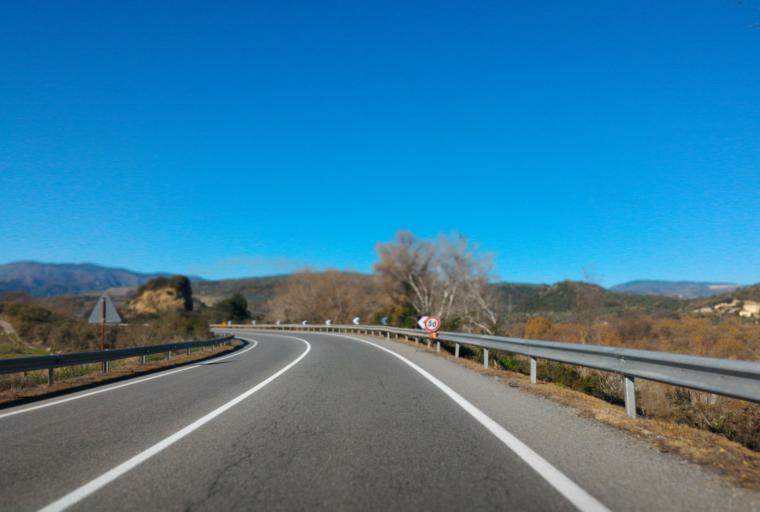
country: IT
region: Calabria
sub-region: Provincia di Crotone
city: Belvedere Spinello
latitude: 39.1911
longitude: 16.8825
